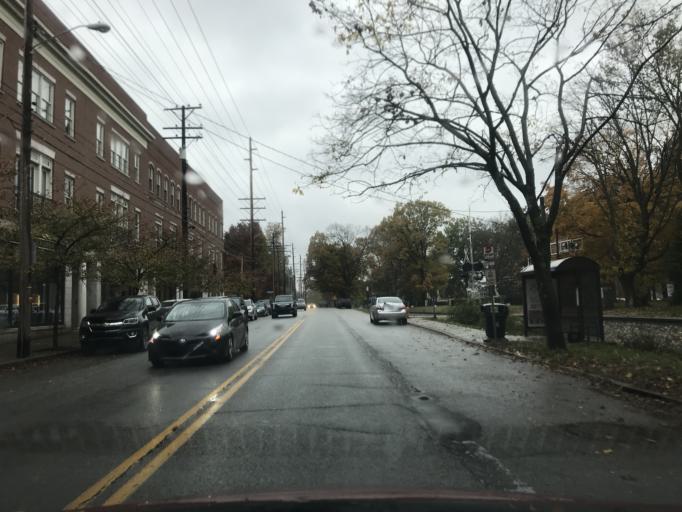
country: US
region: Kentucky
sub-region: Jefferson County
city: Indian Hills
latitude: 38.2547
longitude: -85.6878
